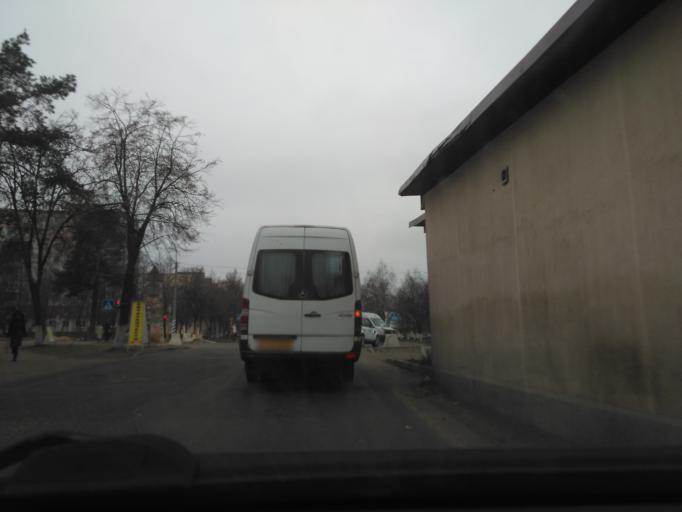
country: BY
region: Minsk
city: Horad Barysaw
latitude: 54.2138
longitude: 28.4892
